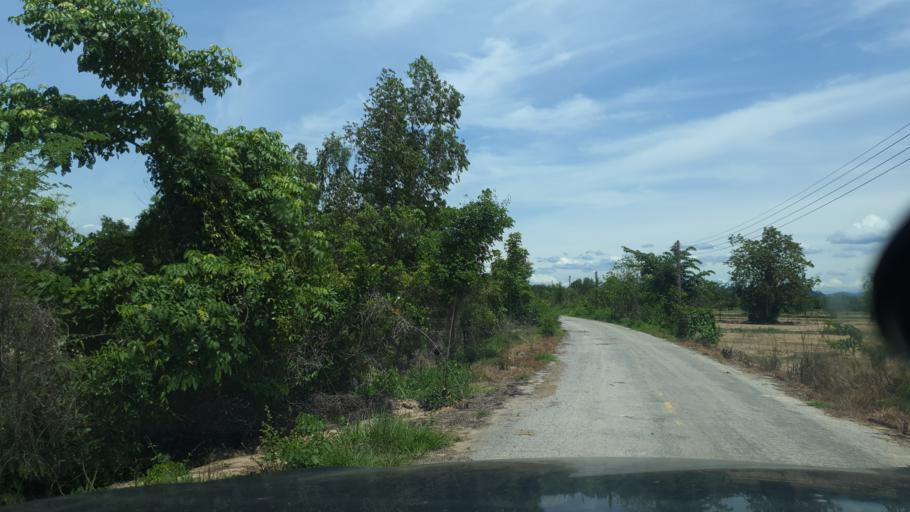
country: TH
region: Sukhothai
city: Ban Dan Lan Hoi
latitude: 17.1505
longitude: 99.6336
